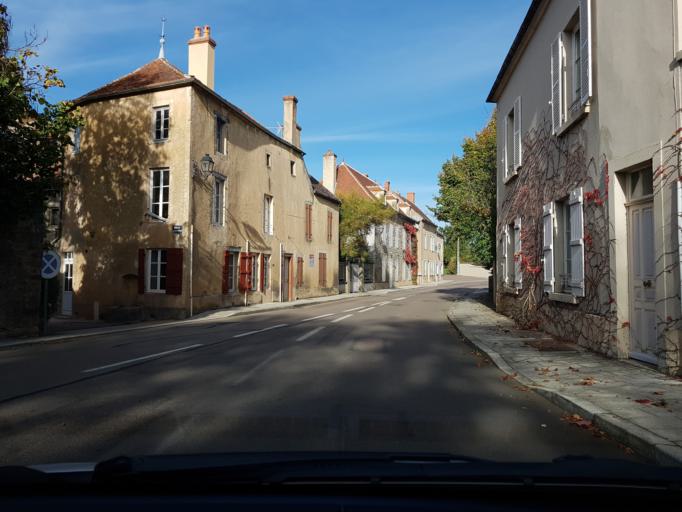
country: FR
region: Bourgogne
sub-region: Departement de la Cote-d'Or
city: Semur-en-Auxois
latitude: 47.5090
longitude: 4.1736
